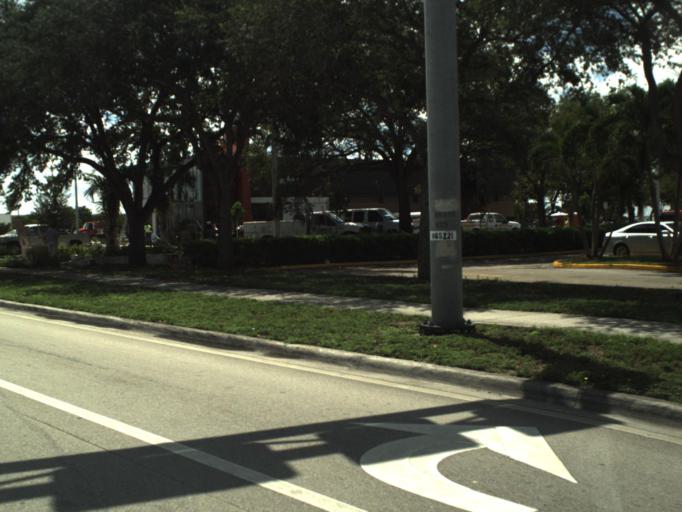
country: US
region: Florida
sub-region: Broward County
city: Pembroke Pines
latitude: 26.0090
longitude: -80.2492
